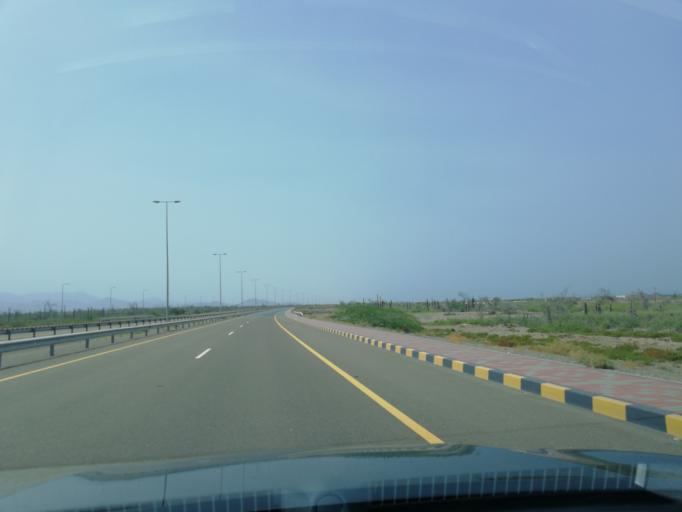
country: OM
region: Al Batinah
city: Shinas
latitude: 24.8722
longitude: 56.4073
